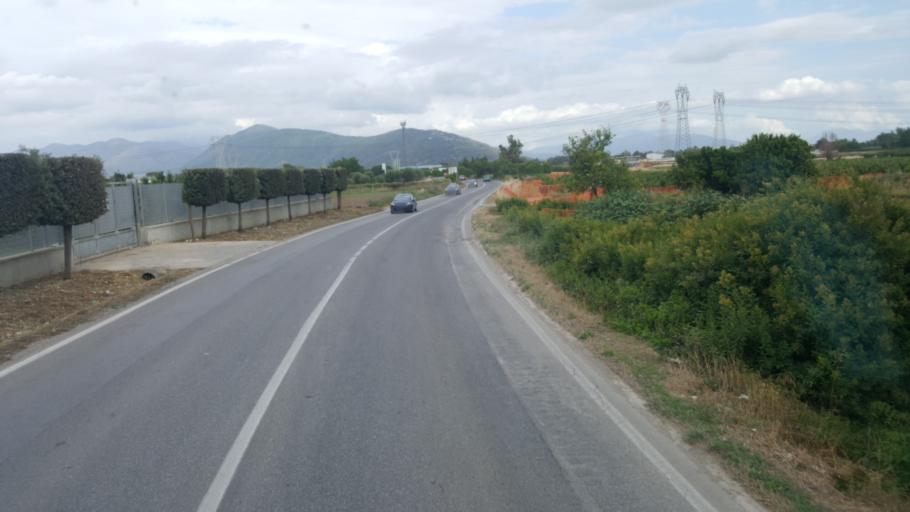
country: IT
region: Campania
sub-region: Provincia di Caserta
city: Maddaloni
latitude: 41.0099
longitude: 14.3852
